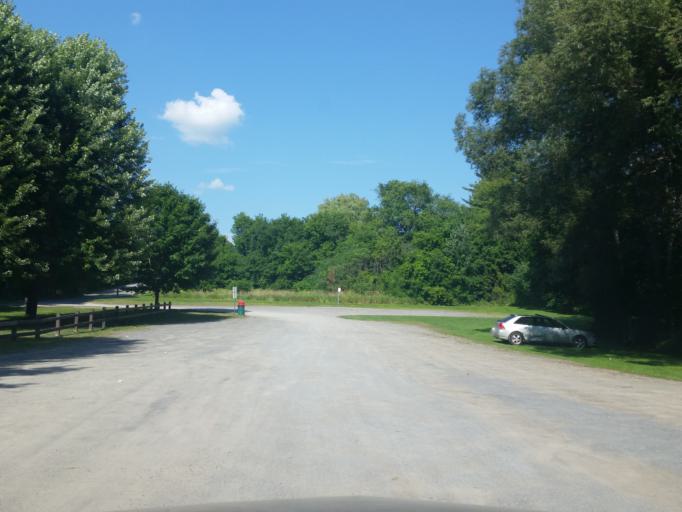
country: CA
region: Ontario
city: Ottawa
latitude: 45.3150
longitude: -75.6963
